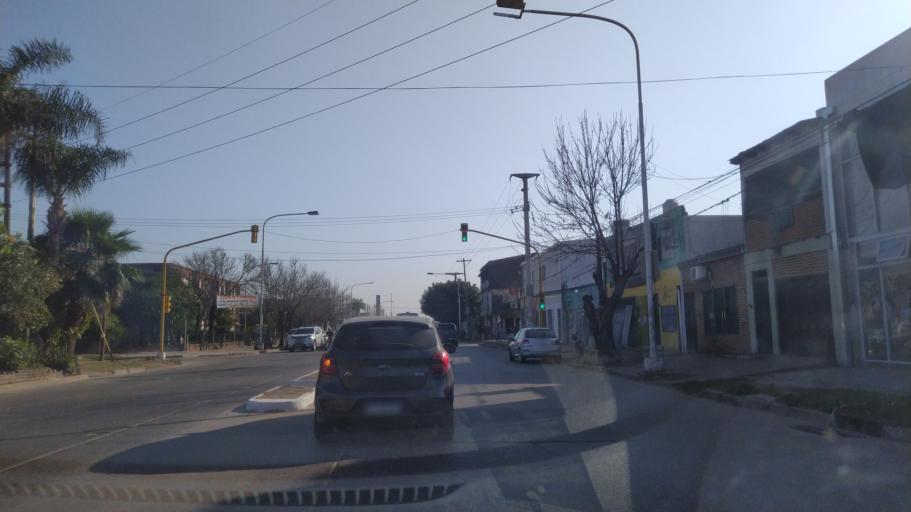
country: AR
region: Corrientes
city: Corrientes
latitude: -27.4810
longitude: -58.8152
